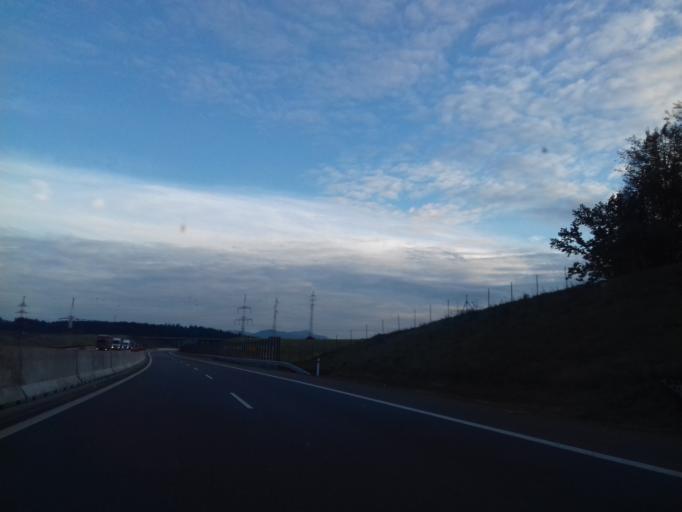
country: SK
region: Trenciansky
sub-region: Okres Povazska Bystrica
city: Povazska Bystrica
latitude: 49.0998
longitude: 18.4154
